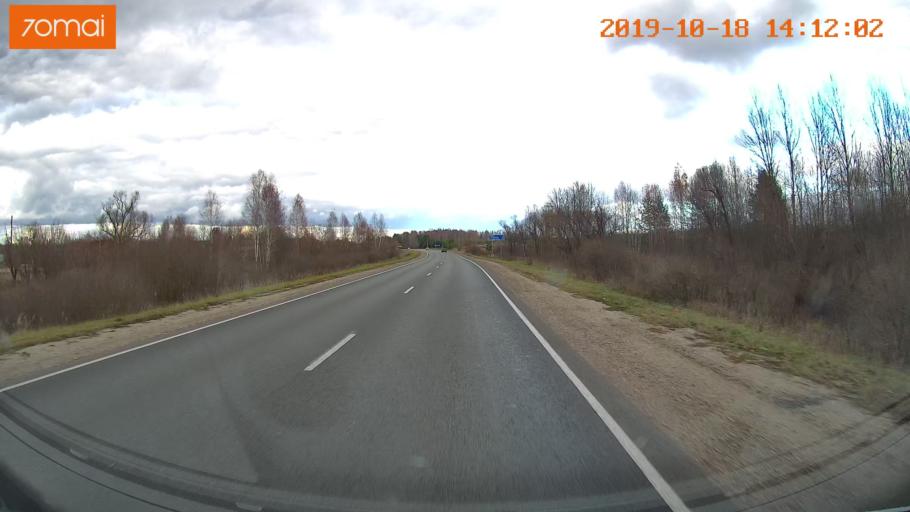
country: RU
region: Rjazan
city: Spas-Klepiki
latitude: 55.1413
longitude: 40.2409
